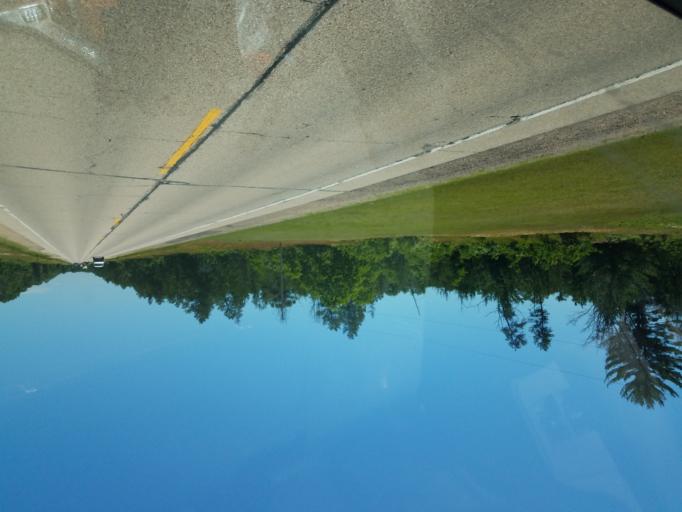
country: US
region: Wisconsin
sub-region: Juneau County
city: New Lisbon
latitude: 44.0361
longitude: -90.0391
